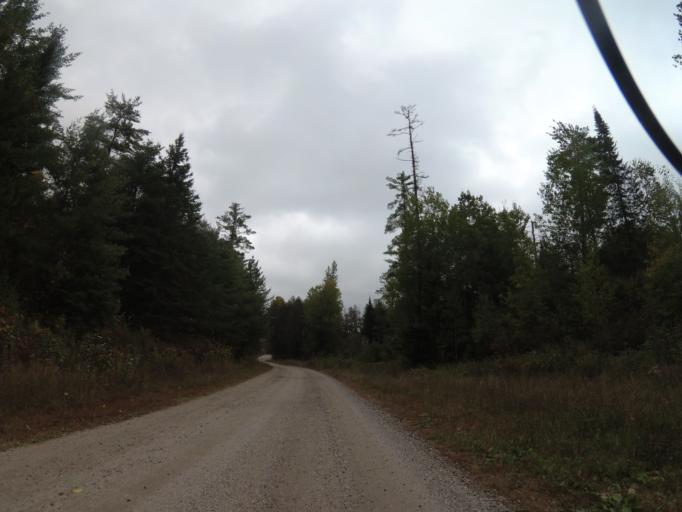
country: CA
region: Ontario
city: Renfrew
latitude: 45.2365
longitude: -77.0402
